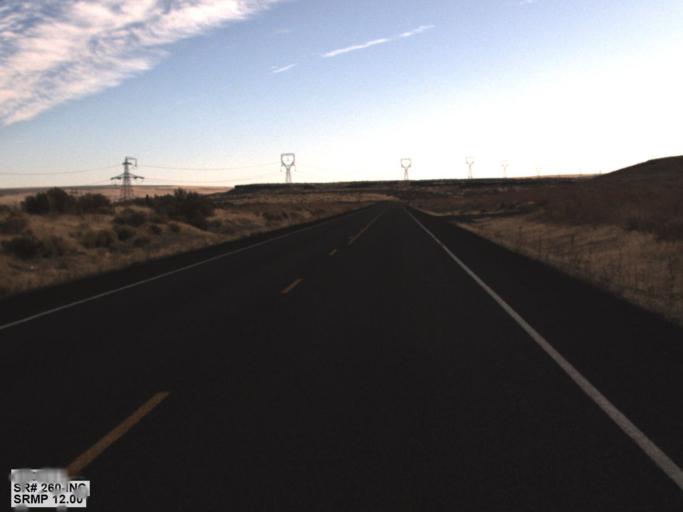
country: US
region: Washington
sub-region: Franklin County
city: Connell
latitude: 46.6346
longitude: -118.7667
